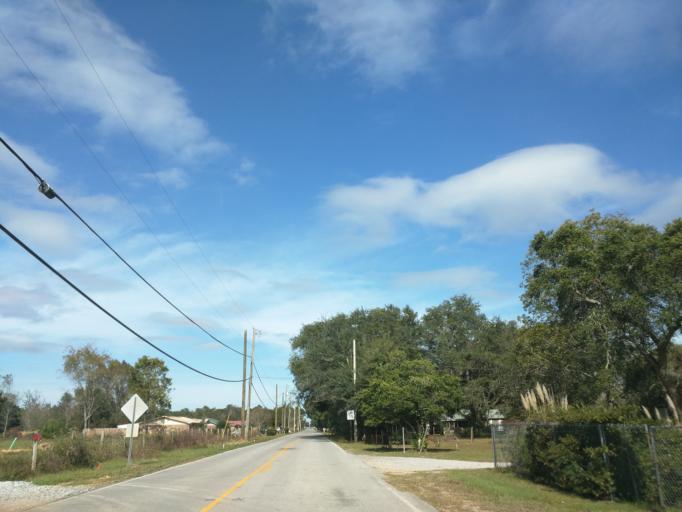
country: US
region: Florida
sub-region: Escambia County
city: Cantonment
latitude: 30.5367
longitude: -87.4060
